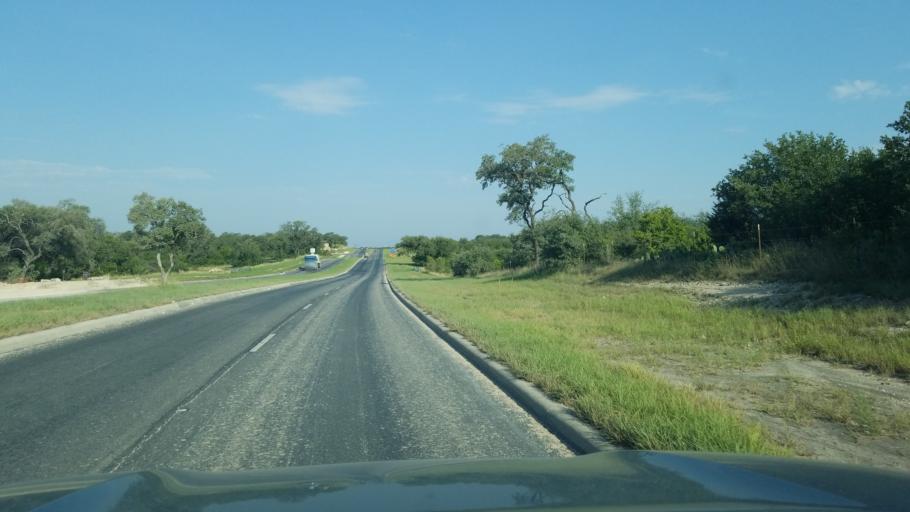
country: US
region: Texas
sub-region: Bexar County
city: Helotes
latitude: 29.4602
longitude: -98.7443
